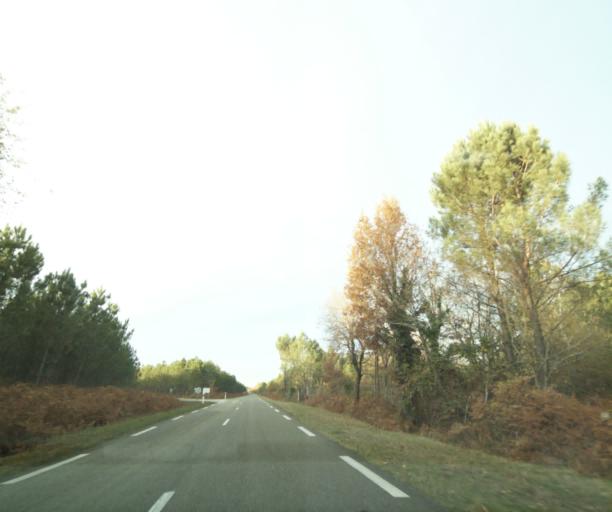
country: FR
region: Aquitaine
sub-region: Departement des Landes
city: Gabarret
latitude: 44.1162
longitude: -0.1045
